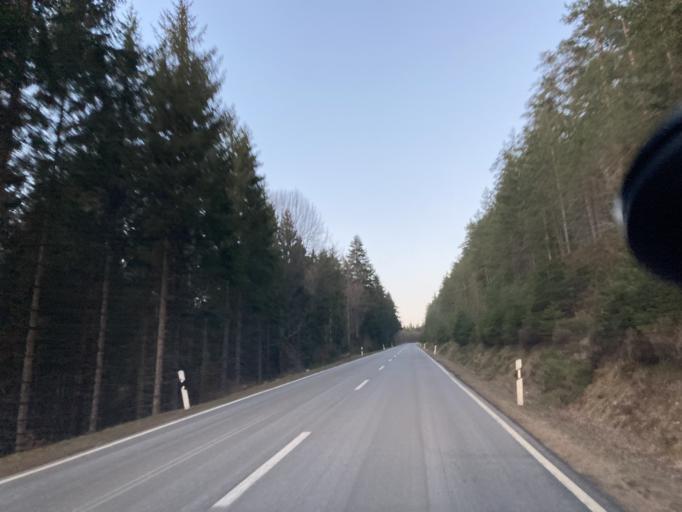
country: DE
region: Baden-Wuerttemberg
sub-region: Karlsruhe Region
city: Neuweiler
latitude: 48.6872
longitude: 8.5847
